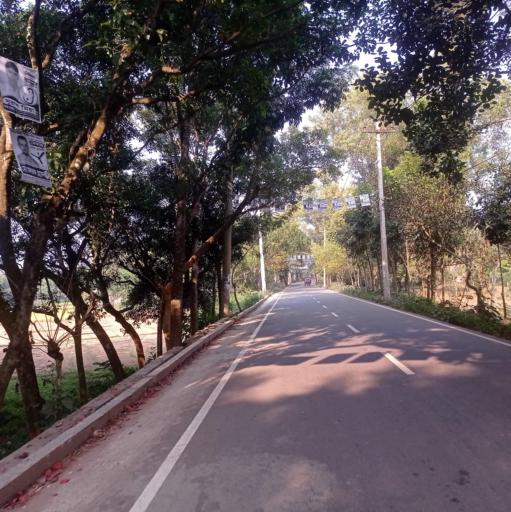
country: BD
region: Dhaka
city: Bhairab Bazar
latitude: 24.0411
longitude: 90.8333
